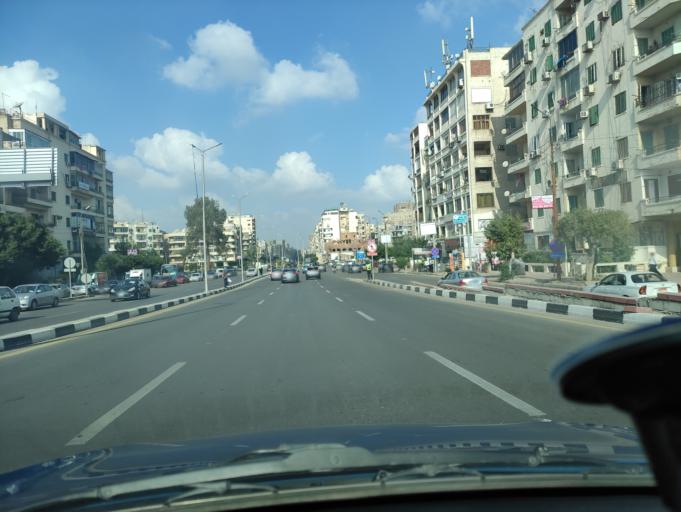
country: EG
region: Muhafazat al Qahirah
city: Cairo
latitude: 30.0987
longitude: 31.3429
